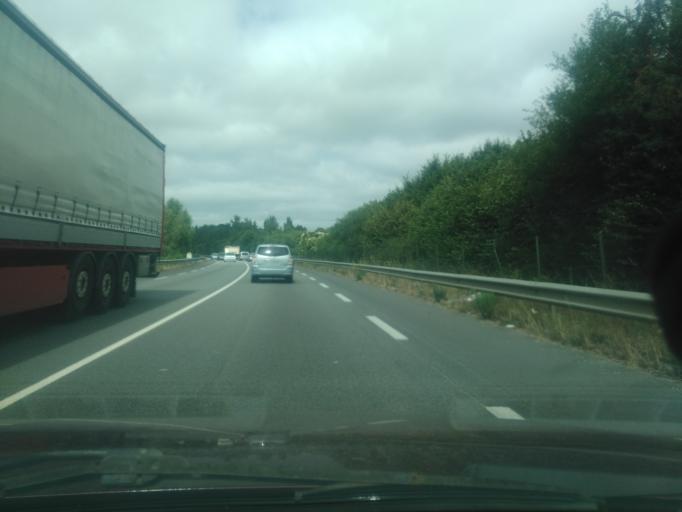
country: FR
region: Pays de la Loire
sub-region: Departement de la Vendee
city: La Roche-sur-Yon
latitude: 46.6912
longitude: -1.4173
